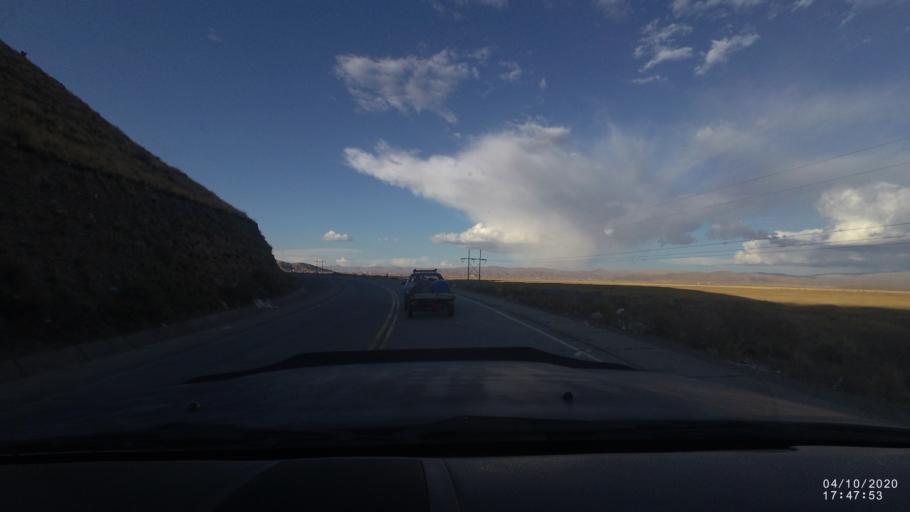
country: BO
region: Oruro
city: Oruro
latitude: -18.0223
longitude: -67.1403
